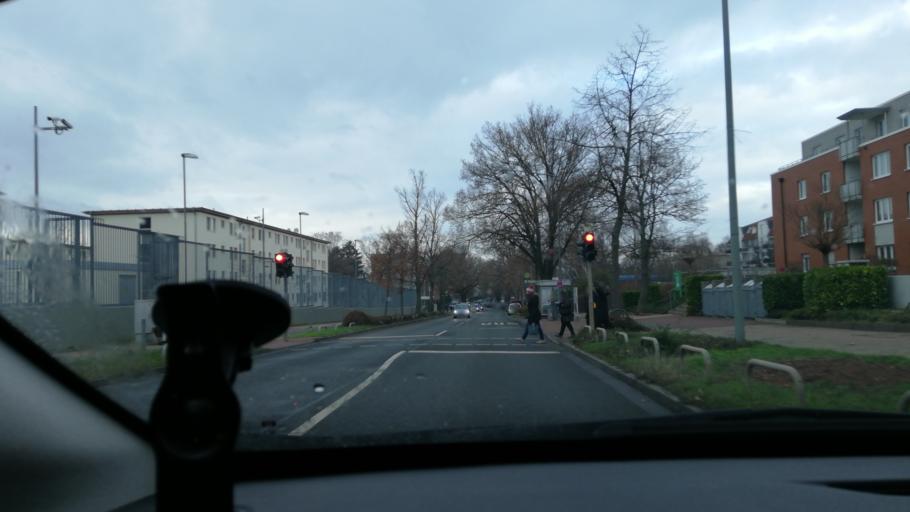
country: DE
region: Hesse
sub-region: Regierungsbezirk Darmstadt
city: Frankfurt am Main
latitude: 50.1420
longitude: 8.6974
